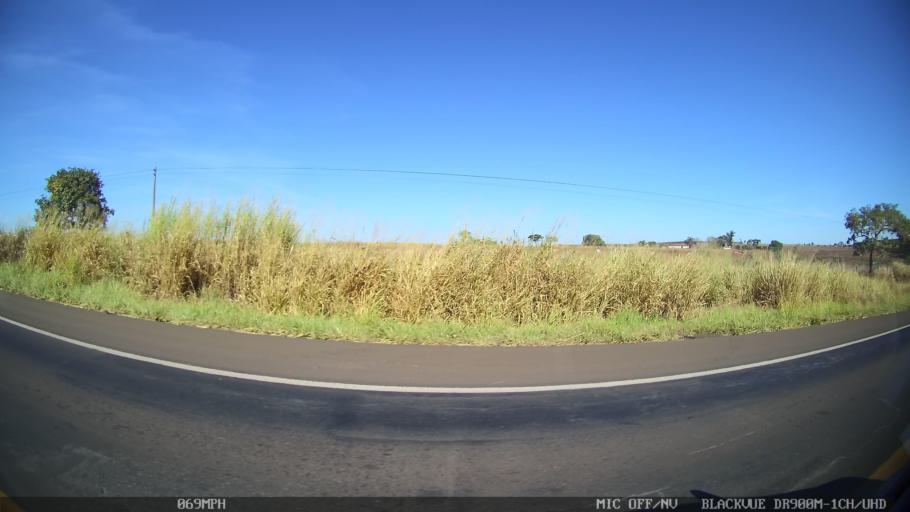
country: BR
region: Sao Paulo
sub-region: Olimpia
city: Olimpia
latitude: -20.6392
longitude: -48.8246
